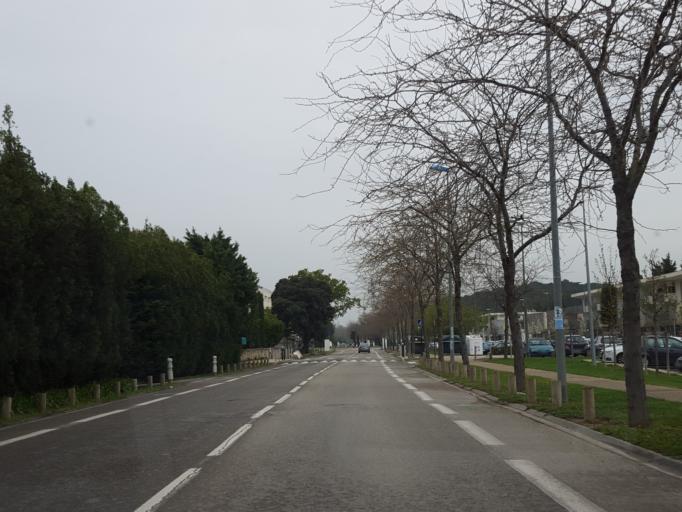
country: FR
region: Provence-Alpes-Cote d'Azur
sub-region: Departement du Vaucluse
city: Montfavet
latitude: 43.9154
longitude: 4.8918
